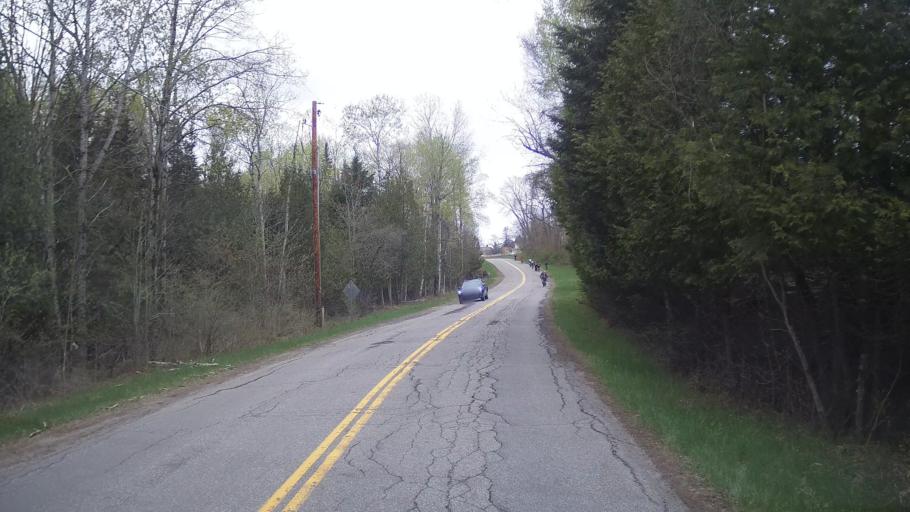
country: US
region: Vermont
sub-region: Caledonia County
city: Lyndonville
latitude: 44.5888
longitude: -71.9542
